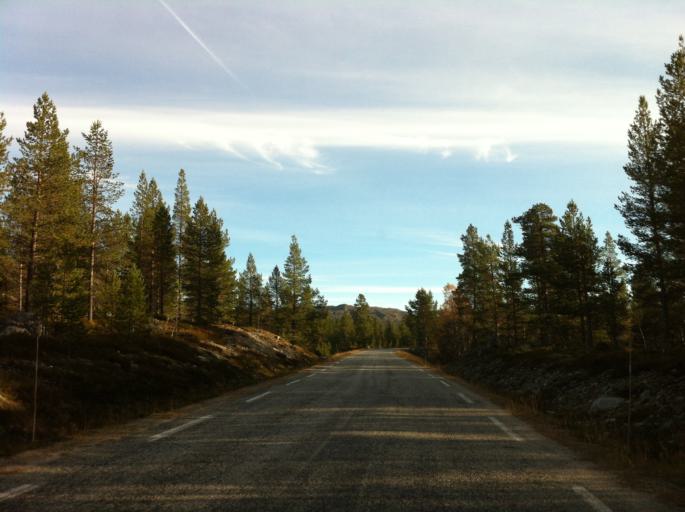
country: NO
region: Hedmark
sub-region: Engerdal
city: Engerdal
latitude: 62.1323
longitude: 11.9861
